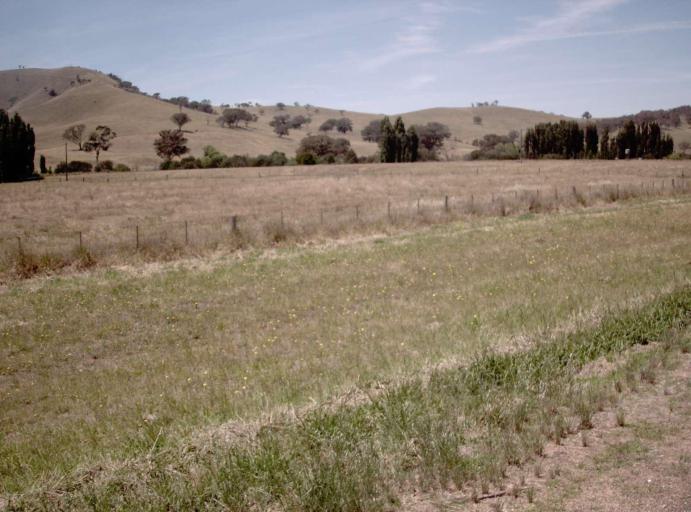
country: AU
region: Victoria
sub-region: East Gippsland
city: Bairnsdale
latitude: -37.2273
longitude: 147.7171
